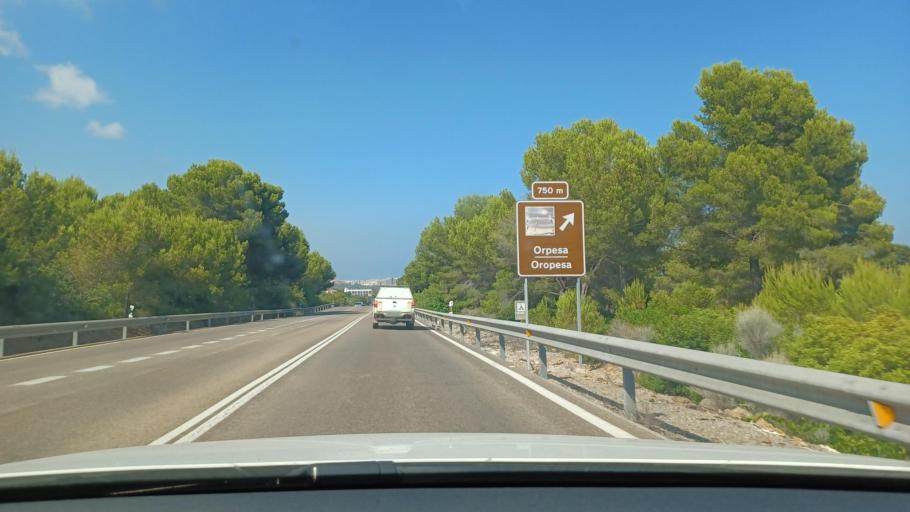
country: ES
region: Valencia
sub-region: Provincia de Castello
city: Orpesa/Oropesa del Mar
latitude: 40.0854
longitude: 0.1221
